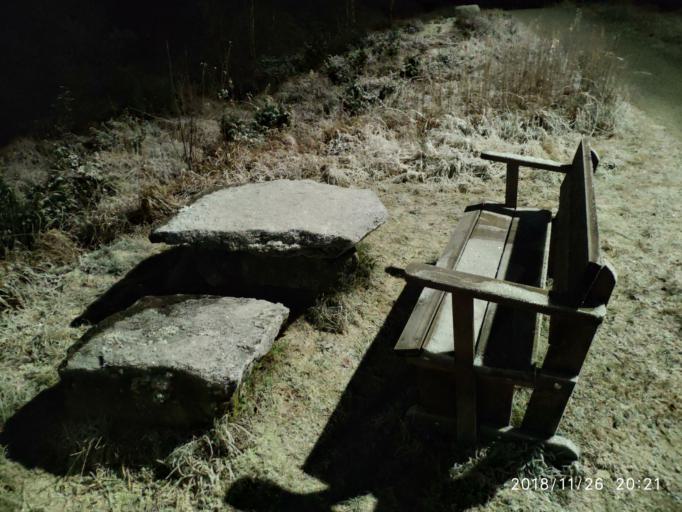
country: NO
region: Rogaland
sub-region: Tysvaer
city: Aksdal
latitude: 59.4199
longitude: 5.4396
